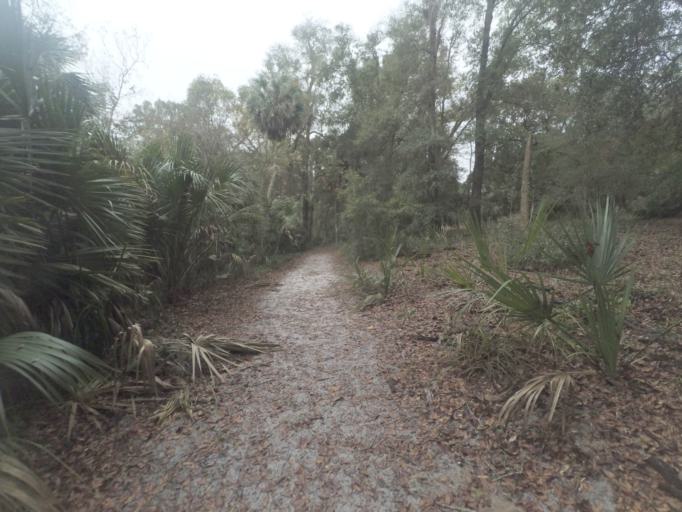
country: US
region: Florida
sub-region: Alachua County
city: Gainesville
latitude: 29.5425
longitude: -82.2912
